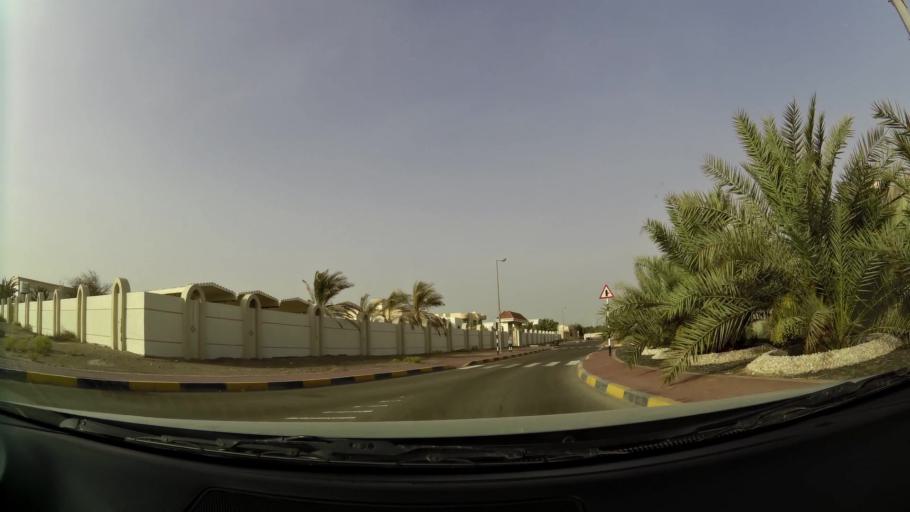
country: AE
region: Abu Dhabi
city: Al Ain
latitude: 24.2190
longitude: 55.6657
